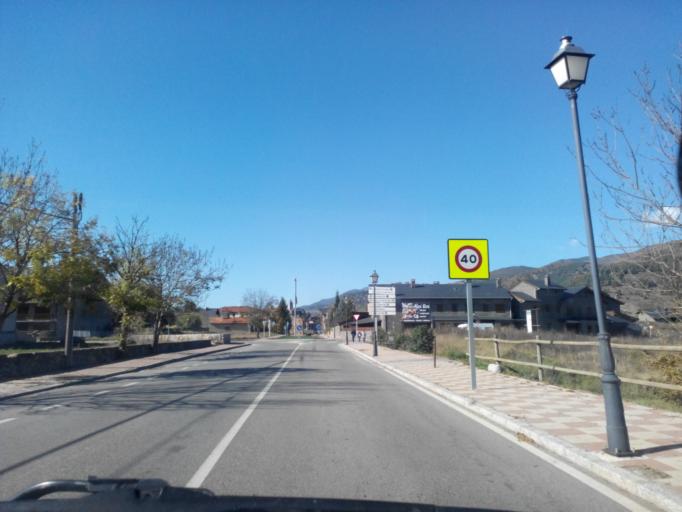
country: ES
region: Catalonia
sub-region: Provincia de Lleida
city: Bellver de Cerdanya
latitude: 42.3697
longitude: 1.7839
